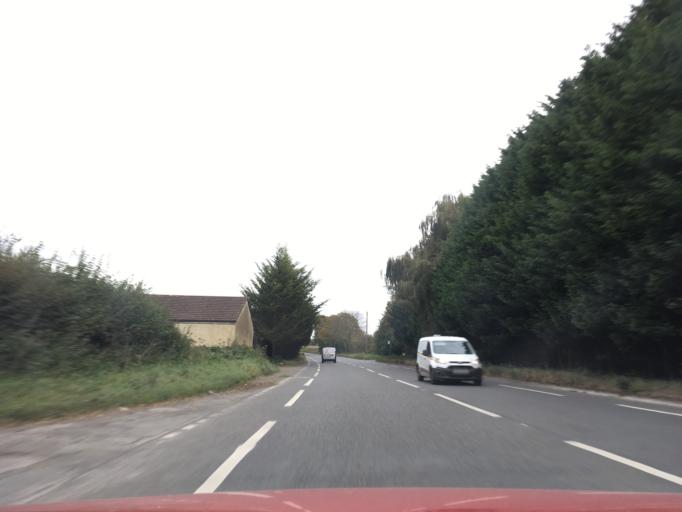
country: GB
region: England
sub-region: Gloucestershire
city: Dursley
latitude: 51.7369
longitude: -2.3597
